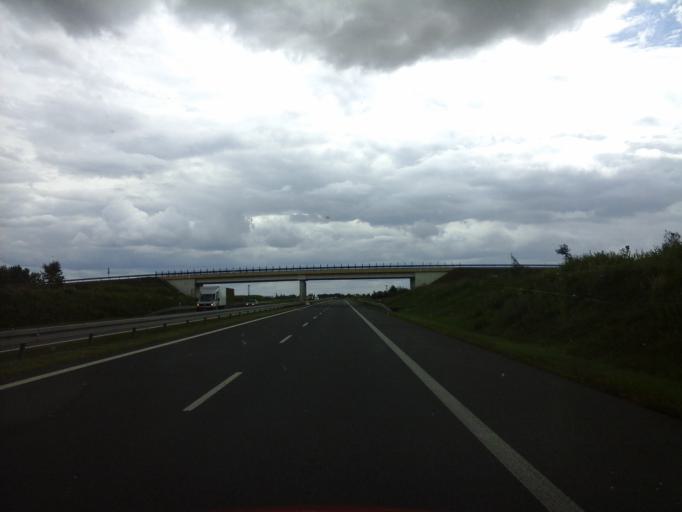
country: PL
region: West Pomeranian Voivodeship
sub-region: Powiat pyrzycki
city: Warnice
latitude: 53.3327
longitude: 14.9588
